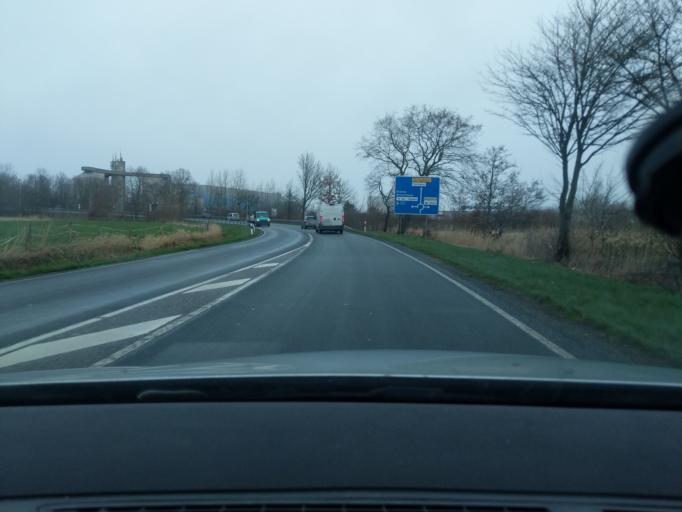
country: DE
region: Lower Saxony
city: Cuxhaven
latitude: 53.8391
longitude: 8.7377
